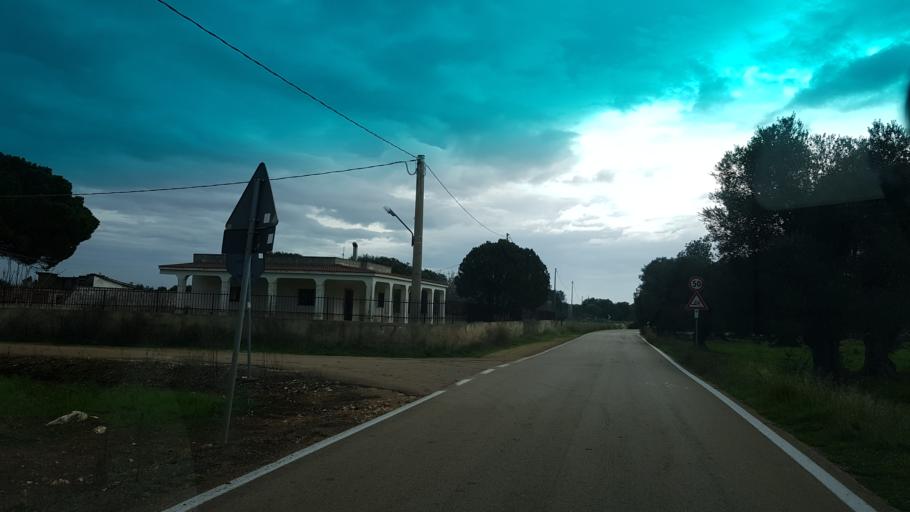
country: IT
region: Apulia
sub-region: Provincia di Brindisi
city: San Vito dei Normanni
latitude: 40.7100
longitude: 17.7665
